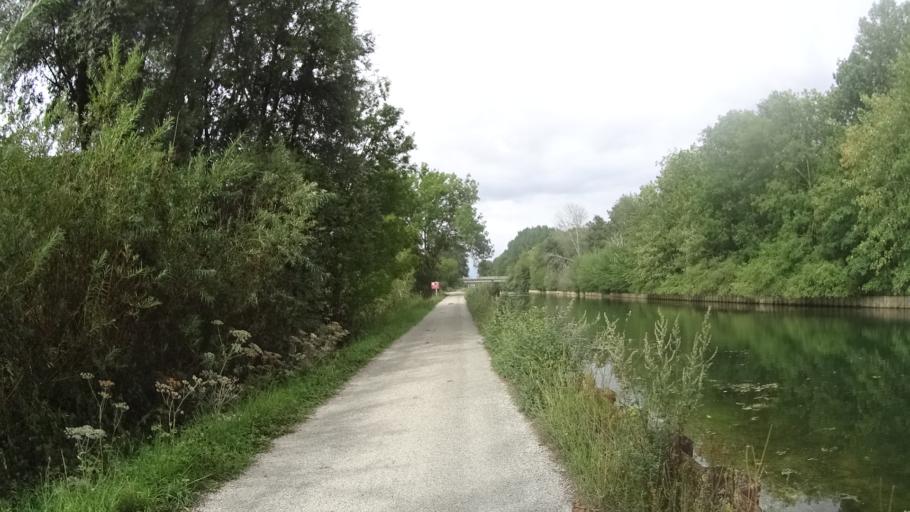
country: FR
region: Picardie
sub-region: Departement de l'Aisne
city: Itancourt
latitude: 49.7608
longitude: 3.3831
